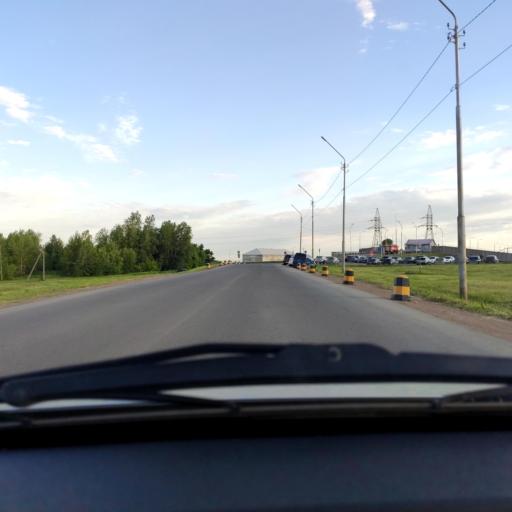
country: RU
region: Bashkortostan
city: Blagoveshchensk
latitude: 54.9077
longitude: 56.0585
